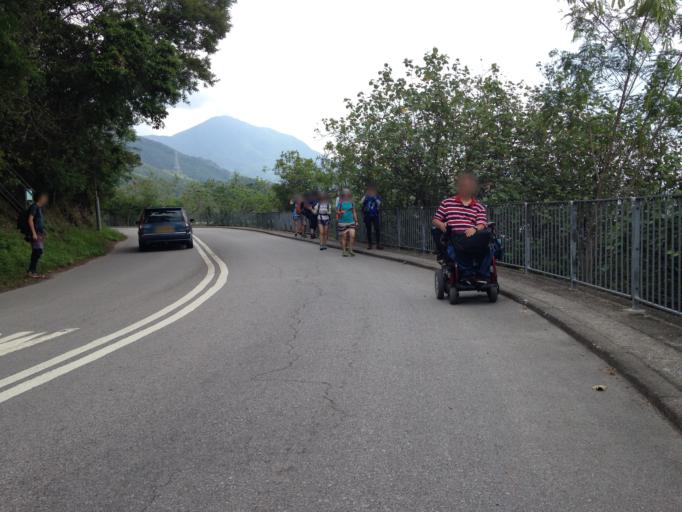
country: CN
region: Guangdong
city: Haishan
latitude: 22.5266
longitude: 114.2084
